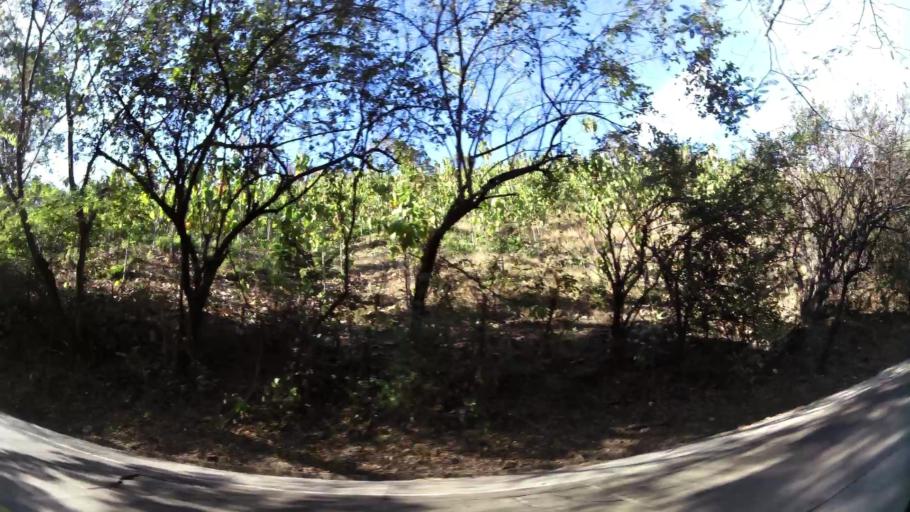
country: SV
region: Santa Ana
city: Texistepeque
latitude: 14.0637
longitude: -89.5070
